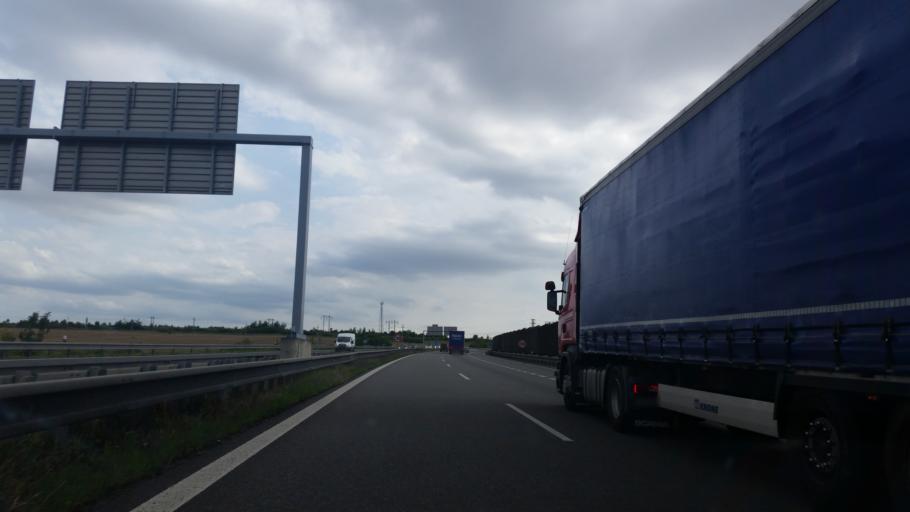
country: CZ
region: South Moravian
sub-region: Okres Vyskov
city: Vyskov
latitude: 49.2777
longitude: 17.0213
